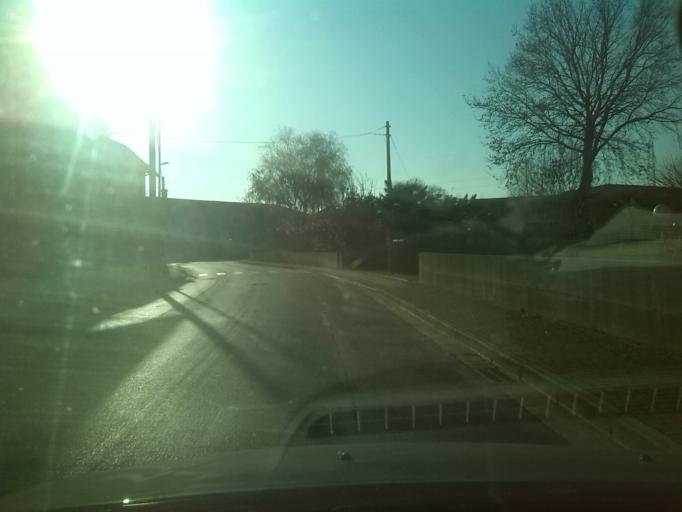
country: IT
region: Friuli Venezia Giulia
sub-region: Provincia di Udine
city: Trivignano Udinese
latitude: 45.9540
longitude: 13.3213
